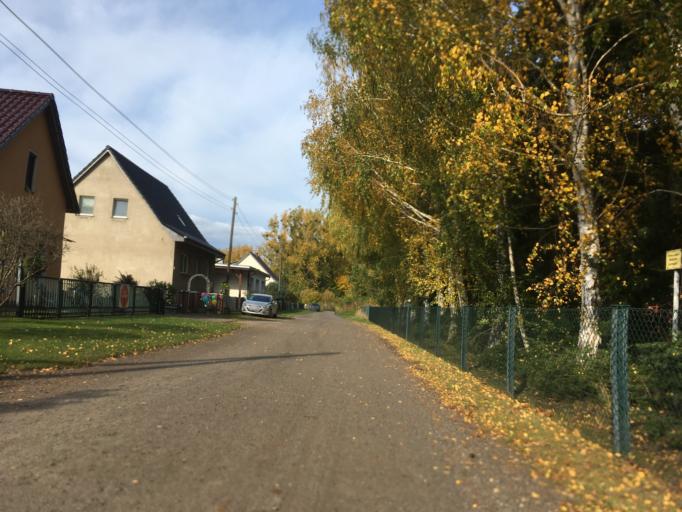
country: DE
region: Brandenburg
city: Zehdenick
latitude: 52.9867
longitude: 13.3546
